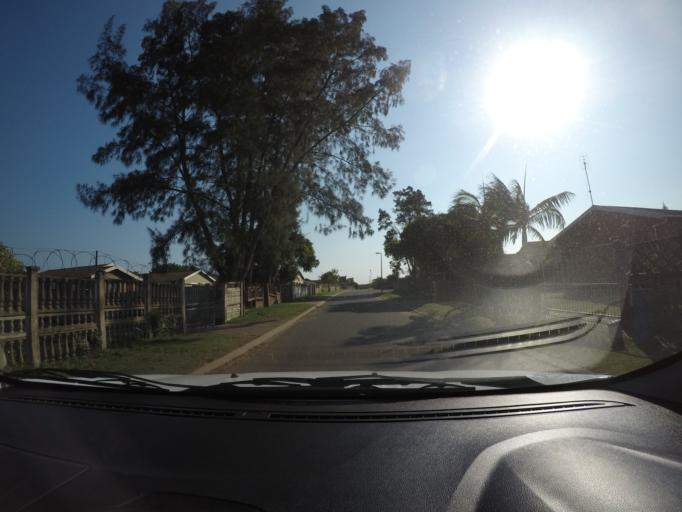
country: ZA
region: KwaZulu-Natal
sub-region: uThungulu District Municipality
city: Richards Bay
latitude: -28.7154
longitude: 32.0387
